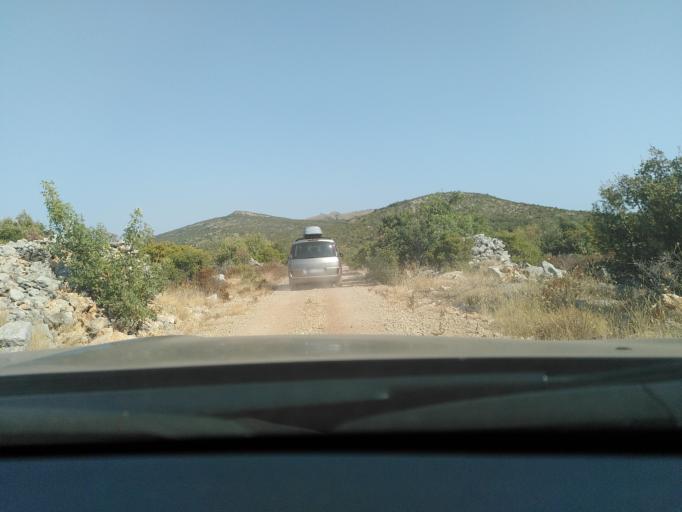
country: HR
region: Splitsko-Dalmatinska
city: Stari Grad
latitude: 43.1622
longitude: 16.5529
